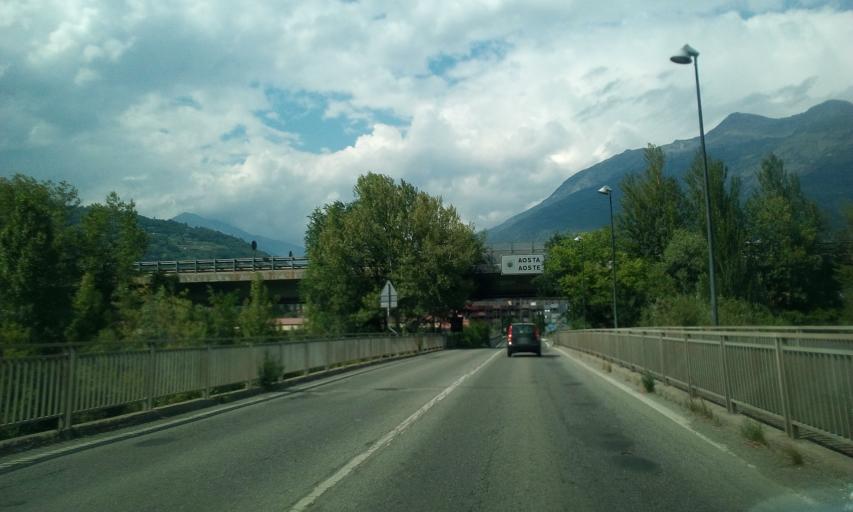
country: IT
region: Aosta Valley
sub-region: Valle d'Aosta
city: Charvensod
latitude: 45.7294
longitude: 7.3220
